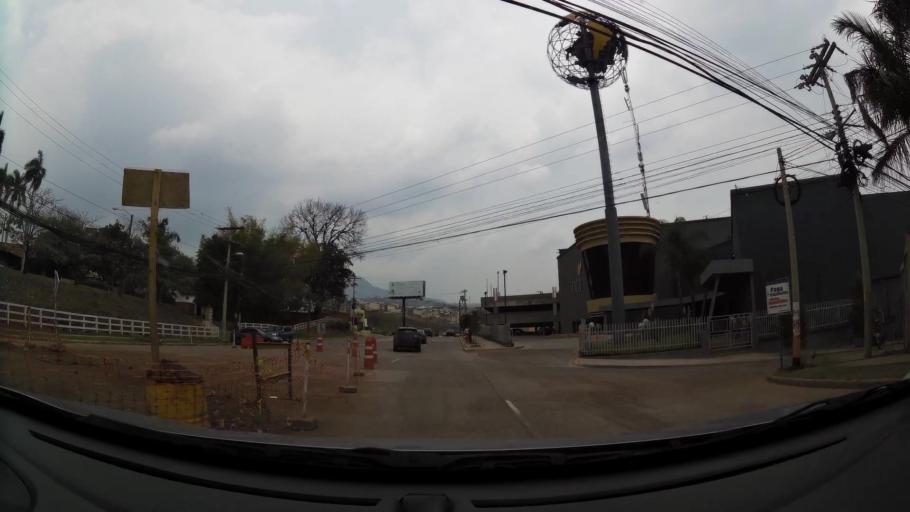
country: HN
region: Francisco Morazan
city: Tegucigalpa
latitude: 14.0827
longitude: -87.1692
